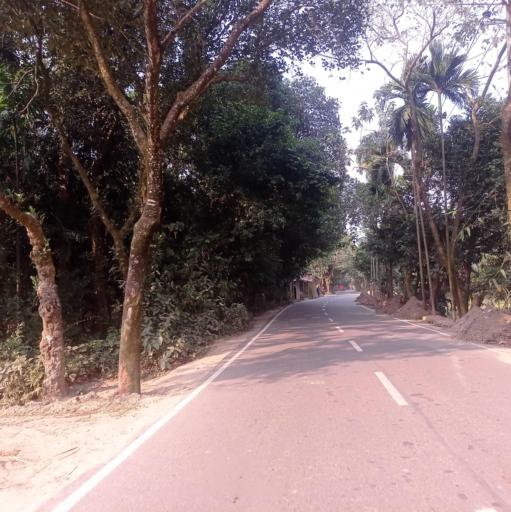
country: BD
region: Dhaka
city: Bhairab Bazar
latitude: 24.0887
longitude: 90.8498
